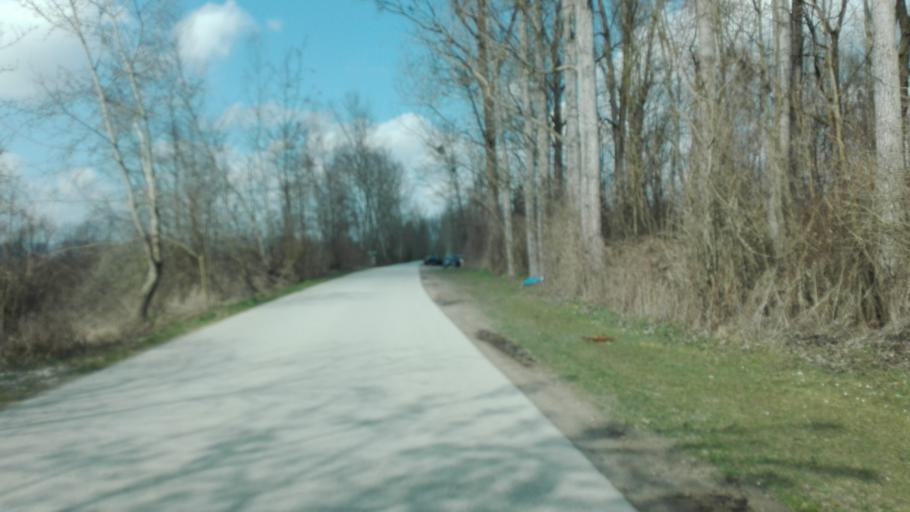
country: AT
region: Upper Austria
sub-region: Politischer Bezirk Urfahr-Umgebung
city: Feldkirchen an der Donau
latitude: 48.3223
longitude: 14.0652
